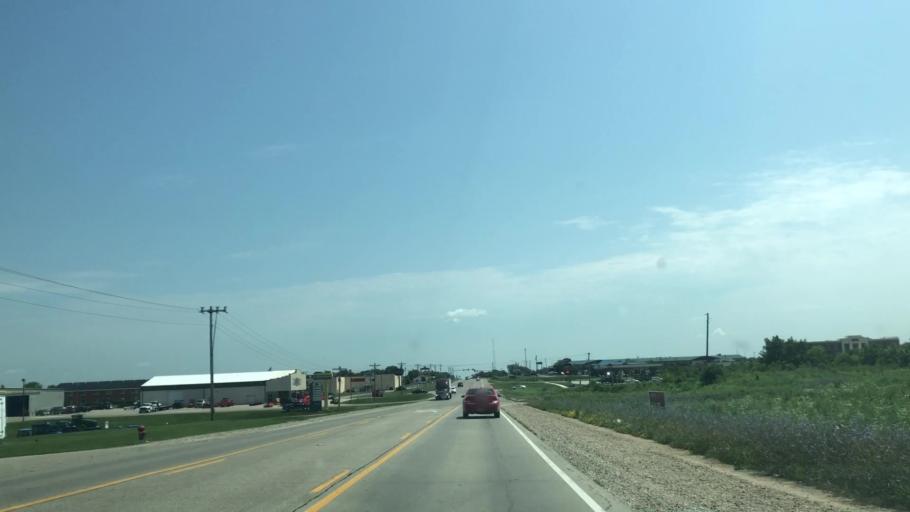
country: US
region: Iowa
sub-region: Marshall County
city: Marshalltown
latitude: 42.0069
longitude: -92.9204
